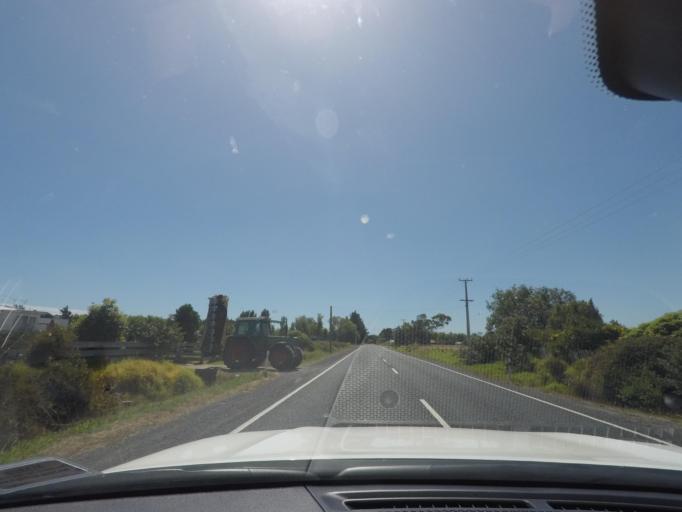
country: NZ
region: Auckland
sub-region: Auckland
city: Parakai
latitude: -36.6389
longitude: 174.3879
